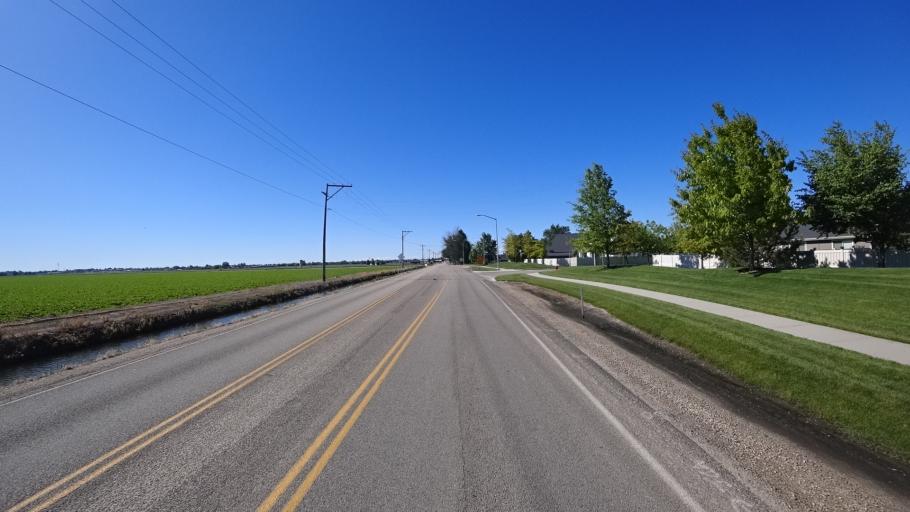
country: US
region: Idaho
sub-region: Ada County
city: Star
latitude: 43.6478
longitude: -116.4538
